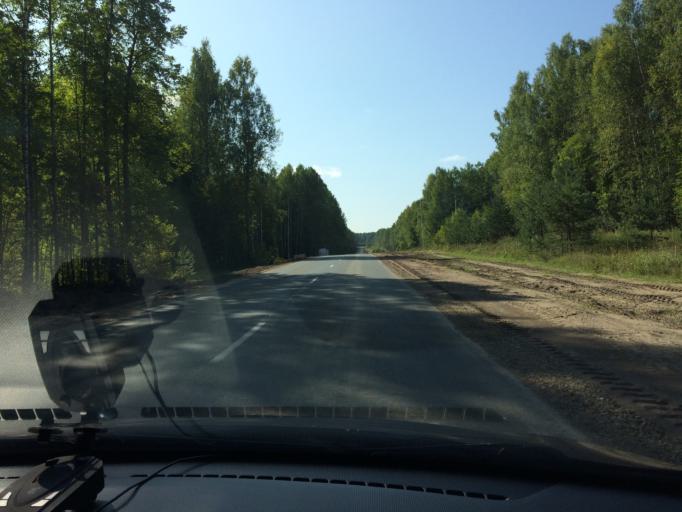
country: RU
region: Mariy-El
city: Sovetskiy
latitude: 56.5580
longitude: 48.4312
